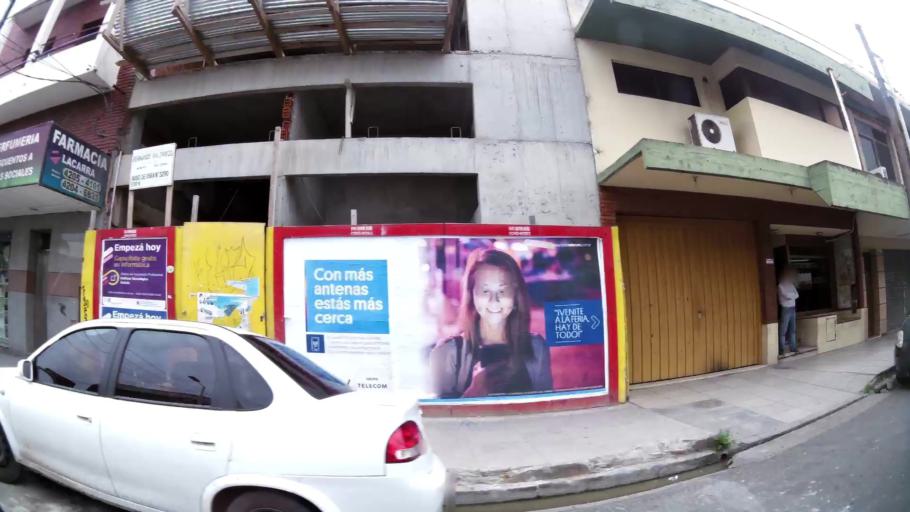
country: AR
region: Buenos Aires
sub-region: Partido de Avellaneda
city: Avellaneda
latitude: -34.6855
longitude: -58.3747
